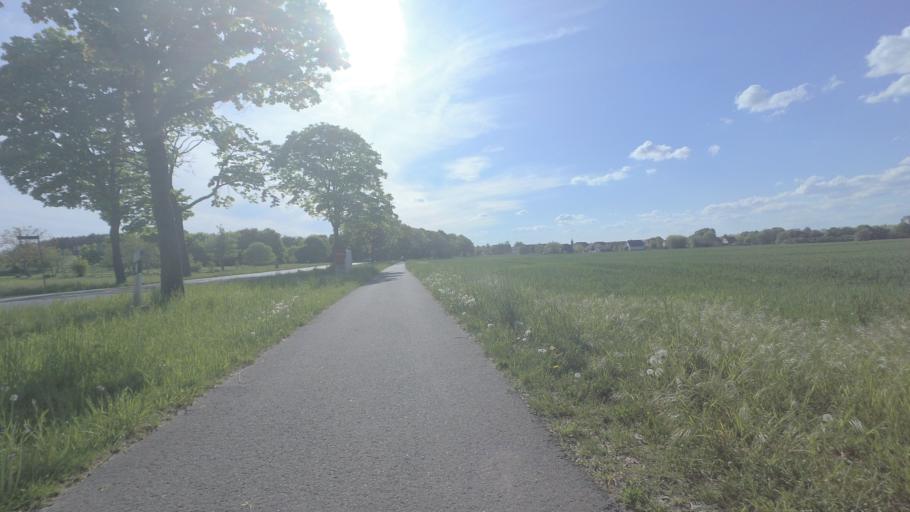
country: DE
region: Brandenburg
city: Mittenwalde
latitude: 52.2594
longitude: 13.5574
